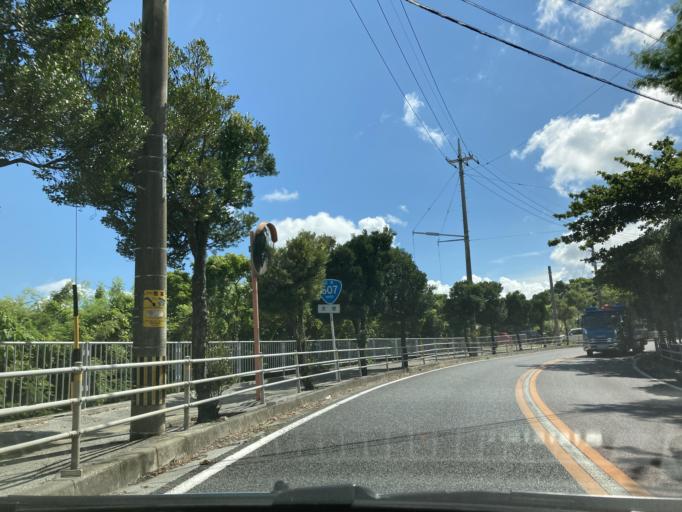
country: JP
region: Okinawa
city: Tomigusuku
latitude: 26.1732
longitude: 127.7204
